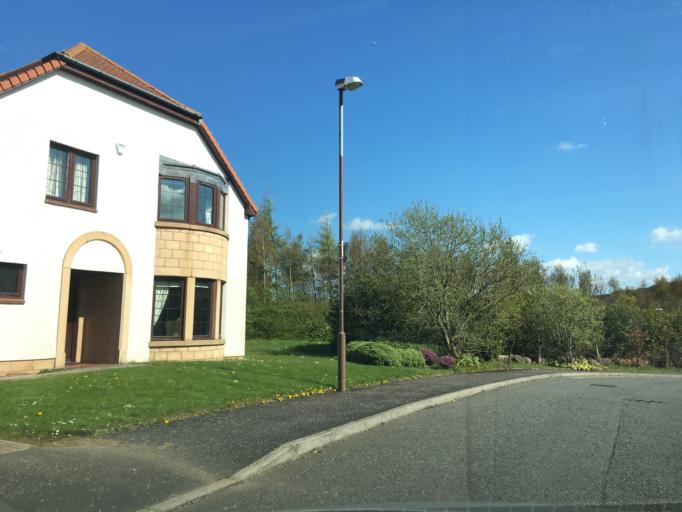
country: GB
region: Scotland
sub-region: Edinburgh
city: Colinton
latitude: 55.9012
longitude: -3.2320
